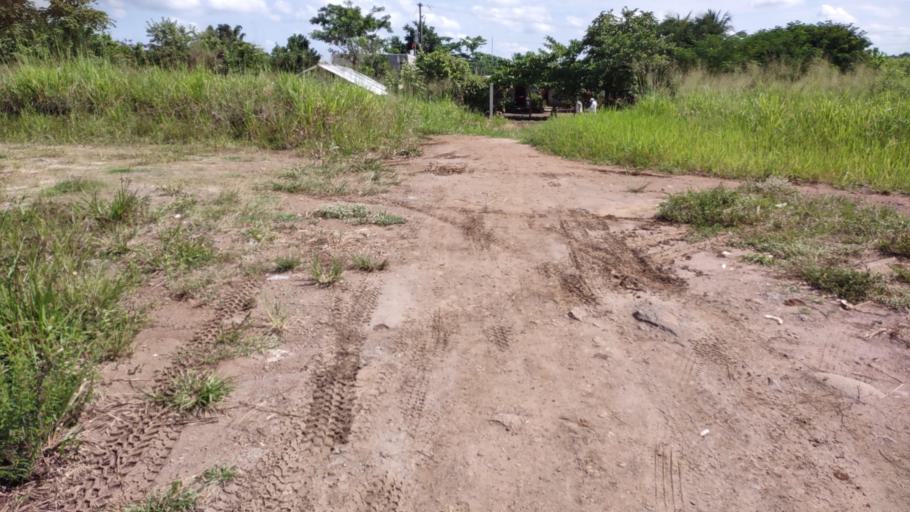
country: MX
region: Veracruz
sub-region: Martinez de la Torre
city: La Union Paso Largo
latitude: 20.1326
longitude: -96.9947
